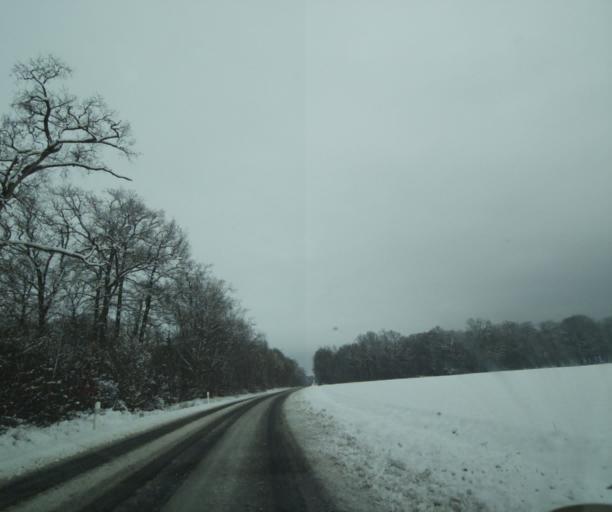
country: FR
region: Champagne-Ardenne
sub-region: Departement de la Haute-Marne
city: Montier-en-Der
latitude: 48.5142
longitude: 4.7467
